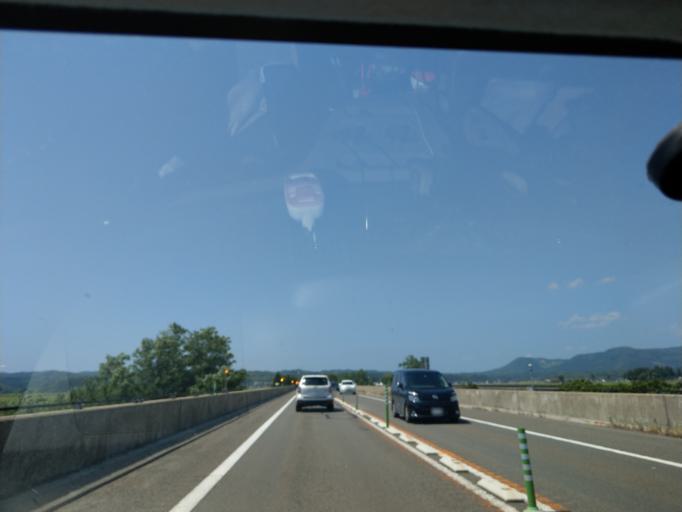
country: JP
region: Akita
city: Omagari
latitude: 39.4019
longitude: 140.4661
